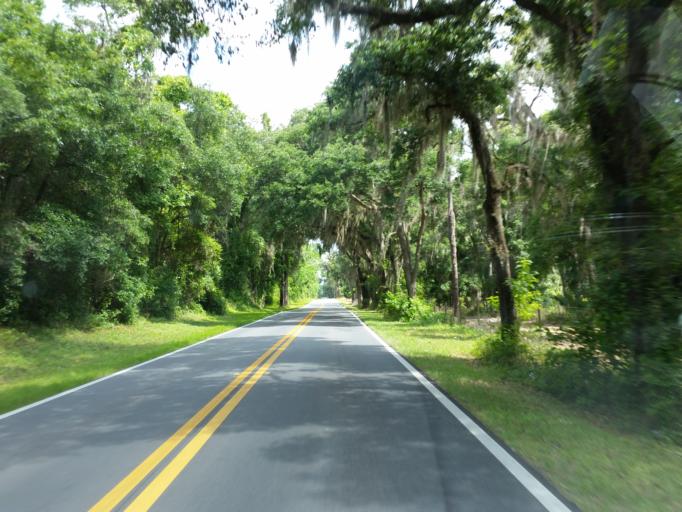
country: US
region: Florida
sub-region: Hernando County
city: North Brooksville
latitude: 28.6179
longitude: -82.3594
